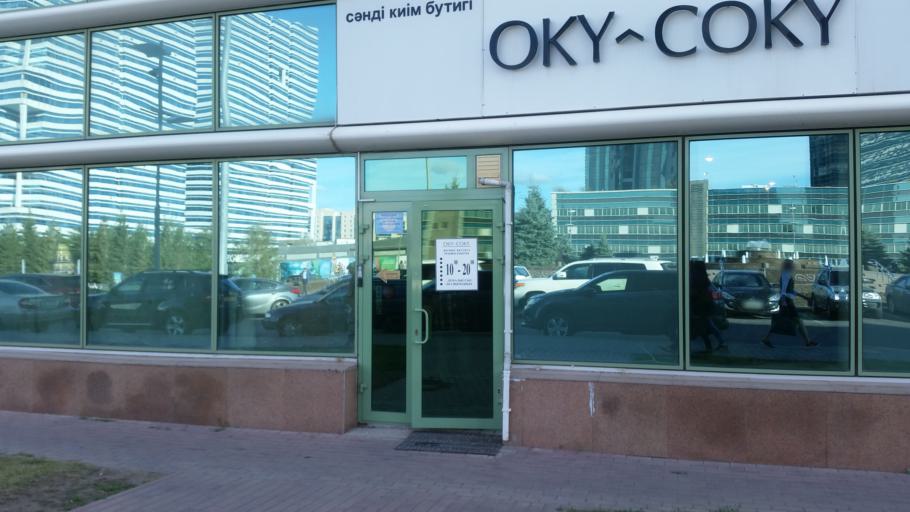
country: KZ
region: Astana Qalasy
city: Astana
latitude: 51.1289
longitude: 71.4229
